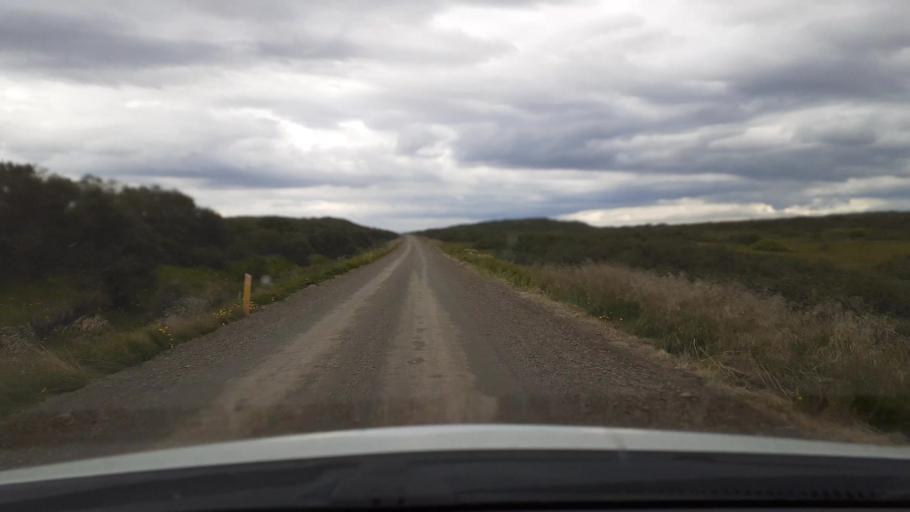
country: IS
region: West
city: Borgarnes
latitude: 64.5987
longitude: -21.9776
